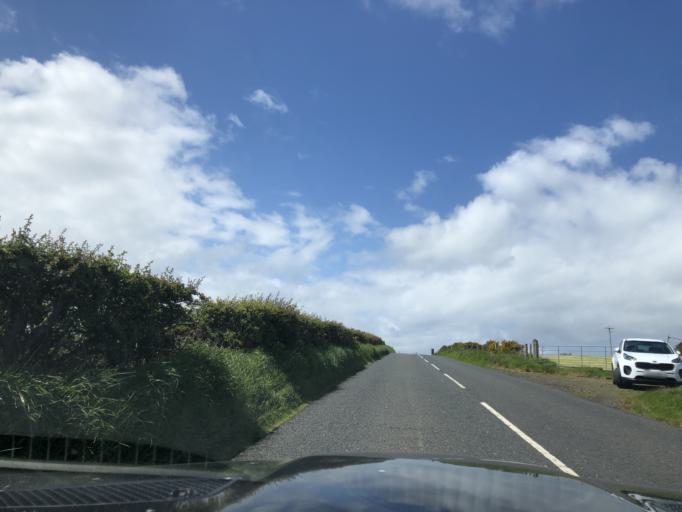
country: GB
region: Northern Ireland
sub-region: Moyle District
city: Ballycastle
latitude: 55.2136
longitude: -6.2802
